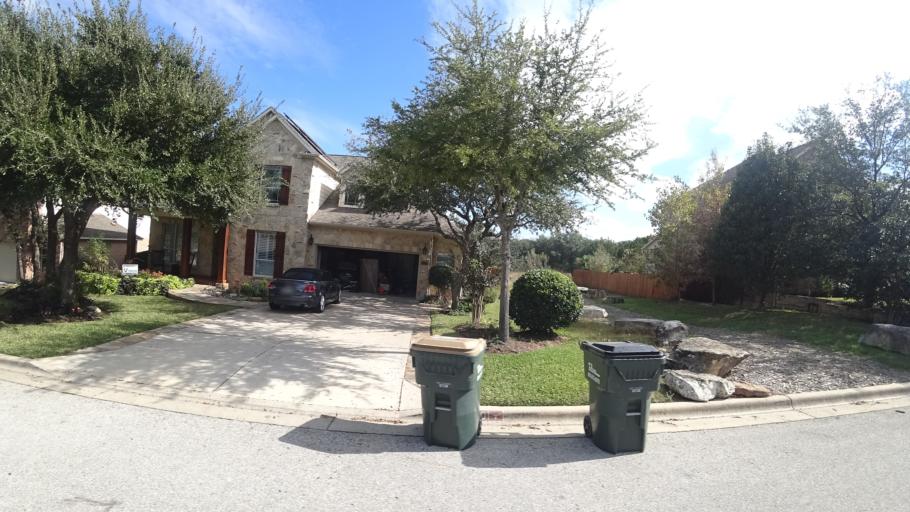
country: US
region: Texas
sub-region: Travis County
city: Hudson Bend
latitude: 30.3683
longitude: -97.9017
